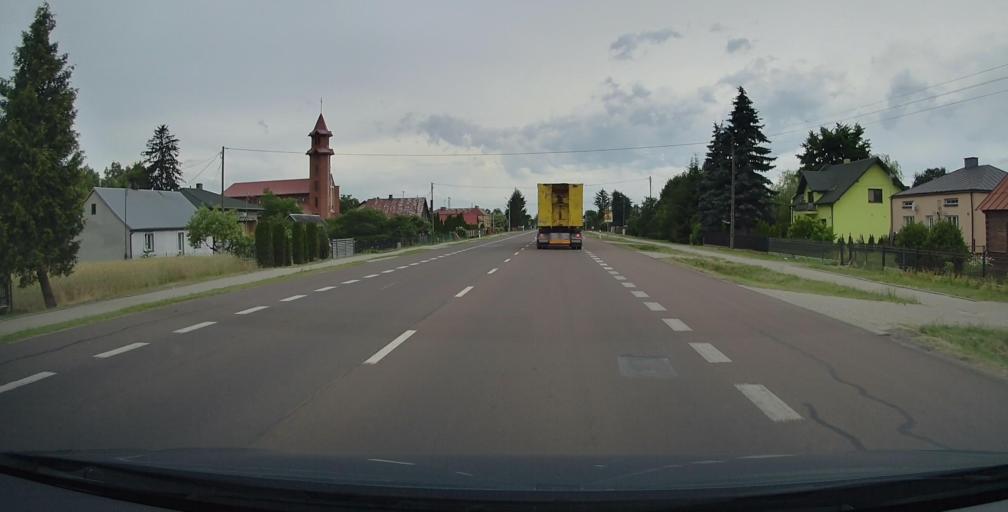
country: PL
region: Lublin Voivodeship
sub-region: Powiat bialski
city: Piszczac
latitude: 52.0375
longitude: 23.4913
